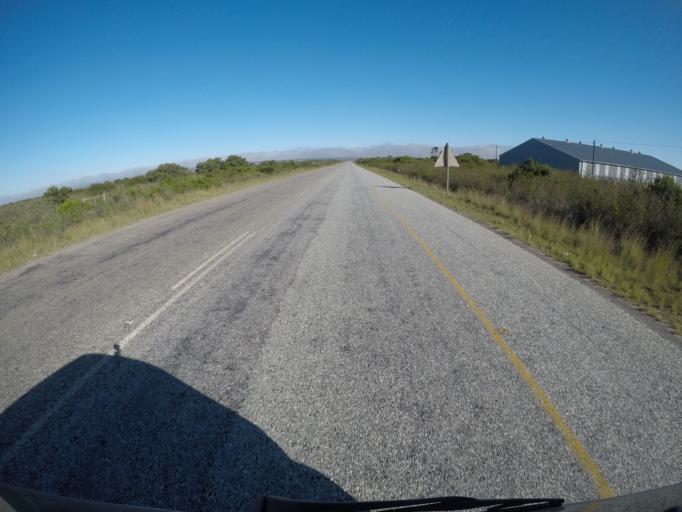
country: ZA
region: Western Cape
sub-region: Eden District Municipality
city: Mossel Bay
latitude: -34.1607
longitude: 22.0097
